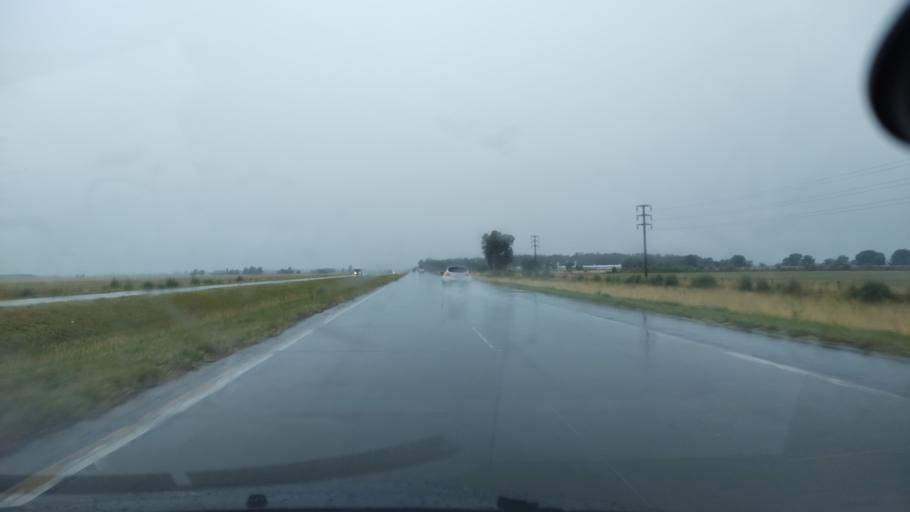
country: AR
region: Buenos Aires
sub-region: Partido de San Vicente
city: San Vicente
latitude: -35.0673
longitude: -58.4972
